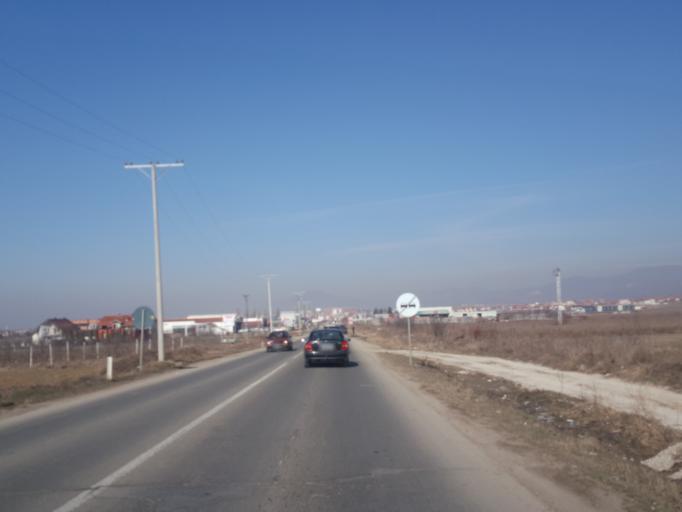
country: XK
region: Mitrovica
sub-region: Vushtrri
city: Vushtrri
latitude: 42.8040
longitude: 20.9923
